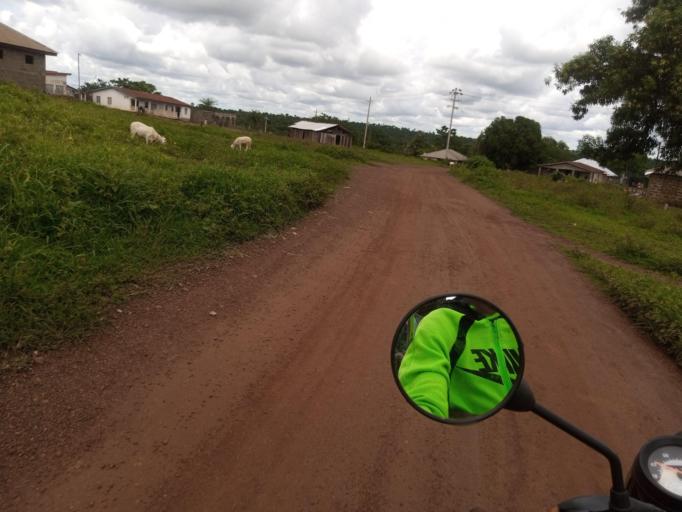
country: SL
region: Northern Province
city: Port Loko
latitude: 8.7610
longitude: -12.7794
